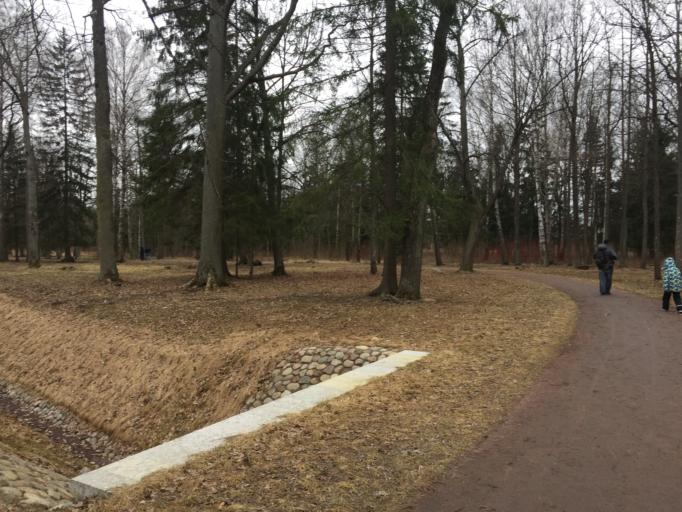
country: RU
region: St.-Petersburg
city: Pushkin
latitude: 59.7231
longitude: 30.3791
